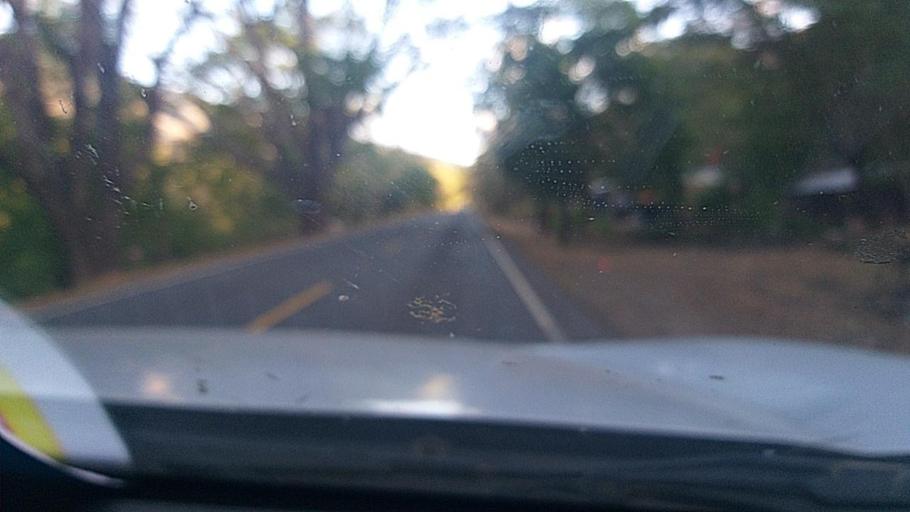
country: NI
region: Esteli
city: Condega
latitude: 13.2973
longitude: -86.3490
